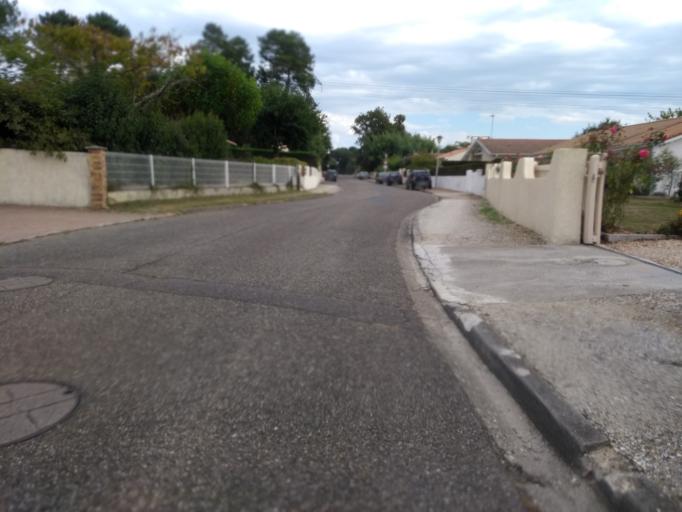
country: FR
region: Aquitaine
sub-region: Departement de la Gironde
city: Cestas
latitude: 44.7345
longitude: -0.6728
